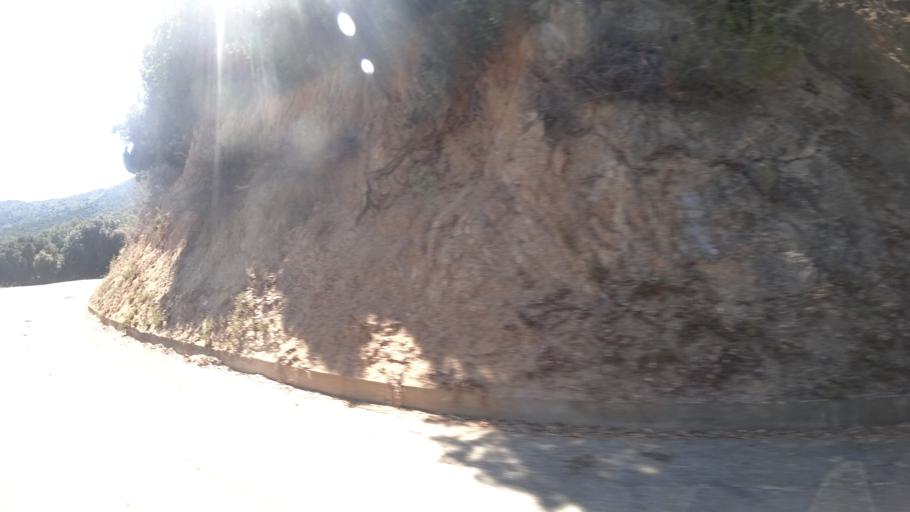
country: FR
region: Corsica
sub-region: Departement de la Corse-du-Sud
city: Alata
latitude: 41.9610
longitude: 8.7274
